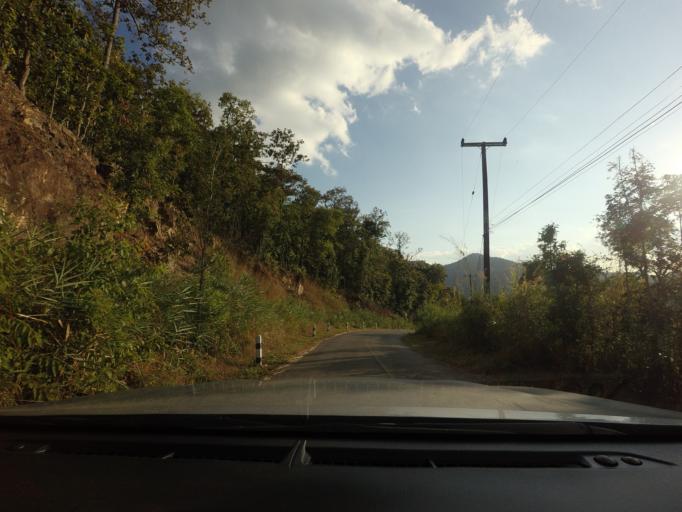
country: TH
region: Chiang Mai
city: Phrao
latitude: 19.4997
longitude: 99.1686
